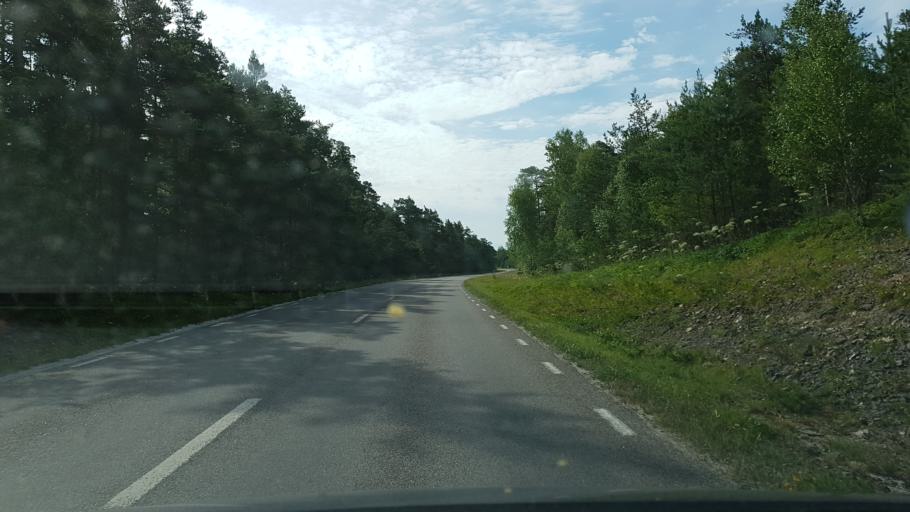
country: SE
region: Gotland
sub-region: Gotland
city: Hemse
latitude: 57.4572
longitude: 18.5766
